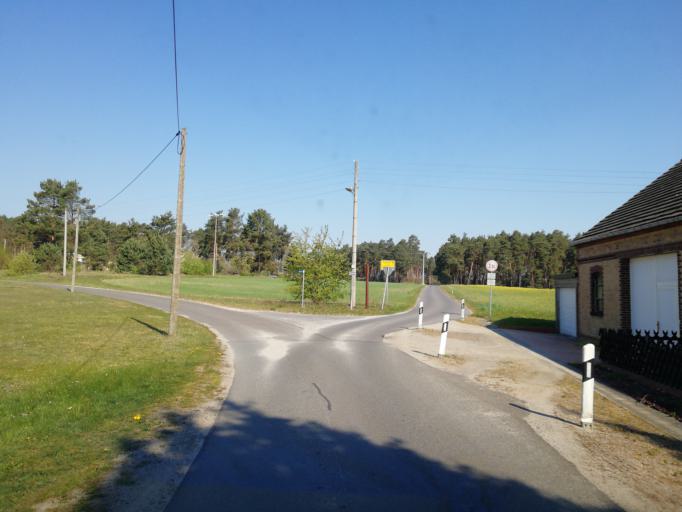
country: DE
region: Brandenburg
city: Sallgast
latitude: 51.6491
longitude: 13.8576
